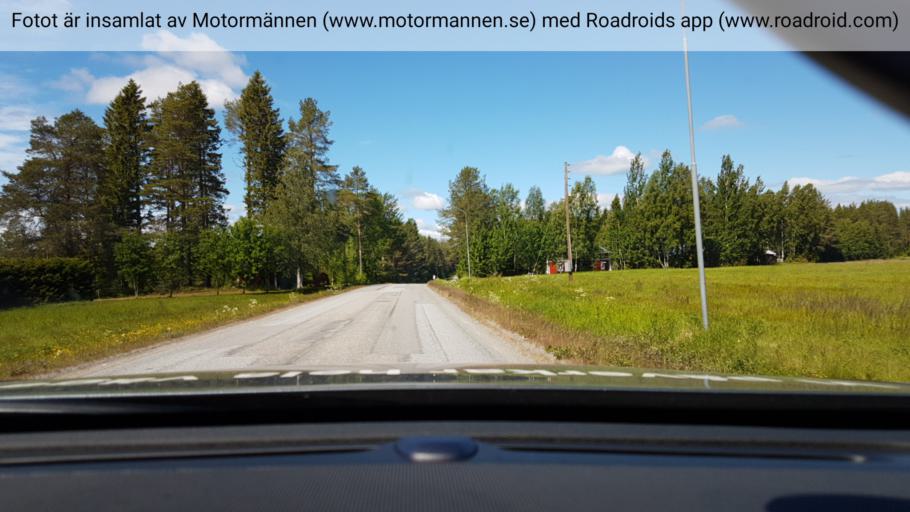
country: SE
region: Vaesterbotten
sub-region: Skelleftea Kommun
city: Burea
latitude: 64.4621
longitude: 21.4060
